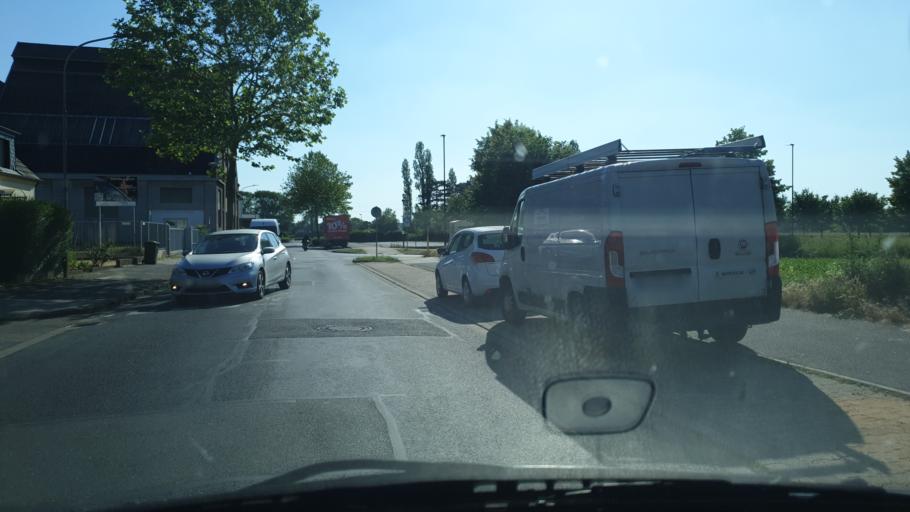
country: DE
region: North Rhine-Westphalia
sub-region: Regierungsbezirk Koln
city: Kerpen
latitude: 50.9000
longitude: 6.6673
